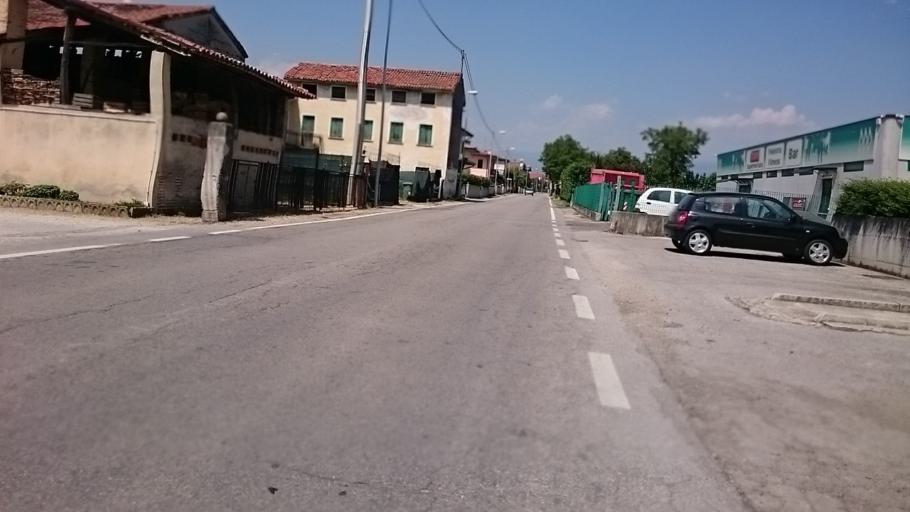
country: IT
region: Veneto
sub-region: Provincia di Vicenza
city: Rosa
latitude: 45.6837
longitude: 11.7401
